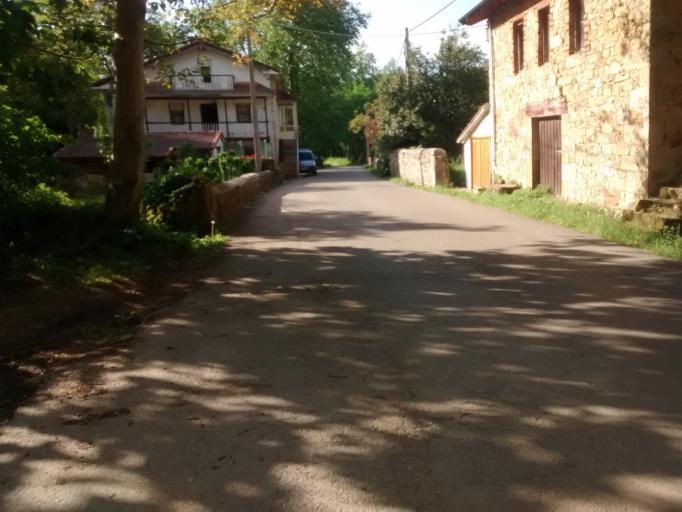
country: ES
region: Cantabria
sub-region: Provincia de Cantabria
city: Entrambasaguas
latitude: 43.3355
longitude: -3.6584
